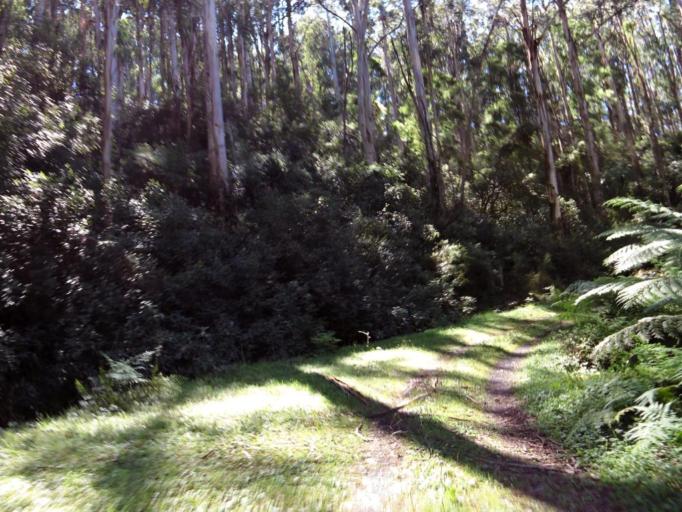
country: AU
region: Victoria
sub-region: Yarra Ranges
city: Yarra Junction
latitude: -37.7445
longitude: 145.6157
